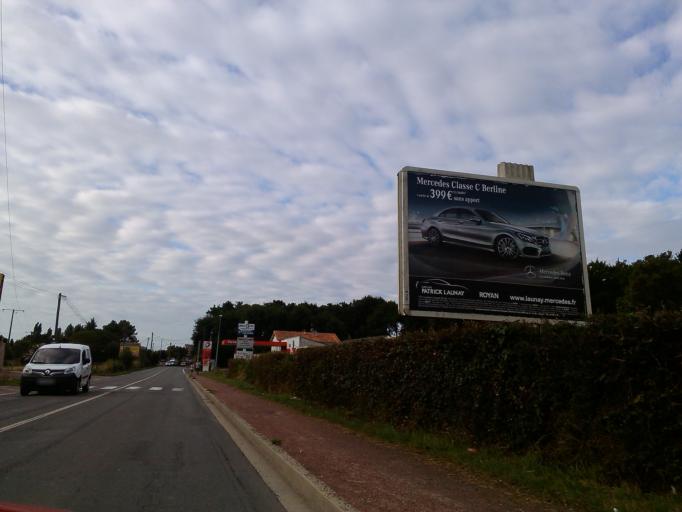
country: FR
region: Poitou-Charentes
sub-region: Departement de la Charente-Maritime
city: Royan
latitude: 45.6477
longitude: -1.0244
